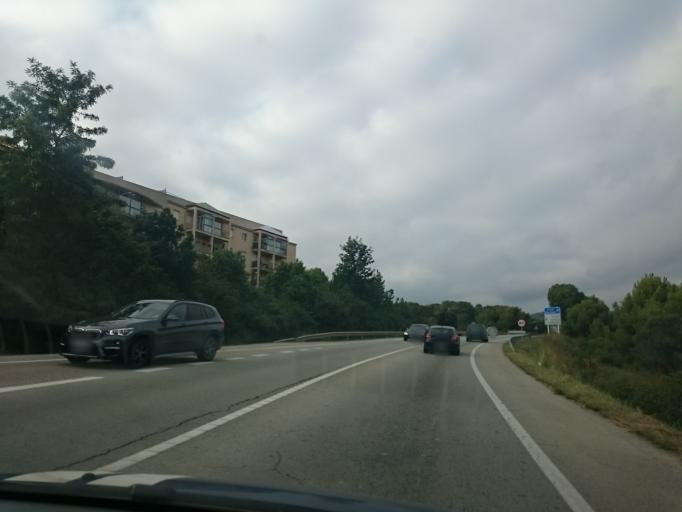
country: ES
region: Catalonia
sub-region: Provincia de Barcelona
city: Sitges
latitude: 41.2404
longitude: 1.8186
